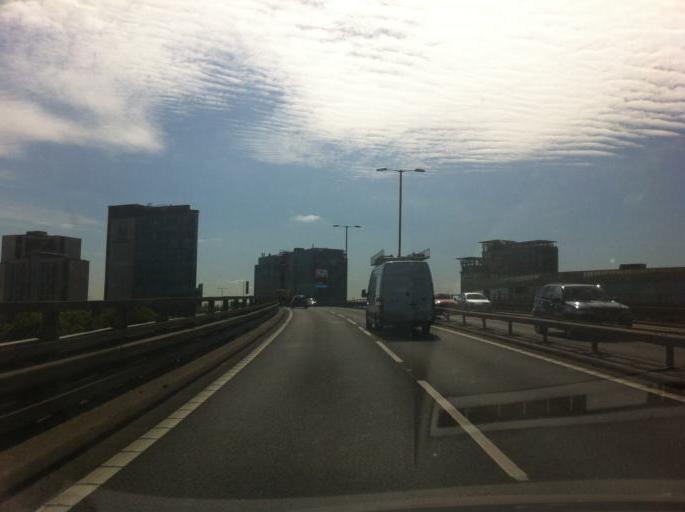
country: GB
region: England
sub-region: Greater London
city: Brentford
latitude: 51.4899
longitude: -0.3179
